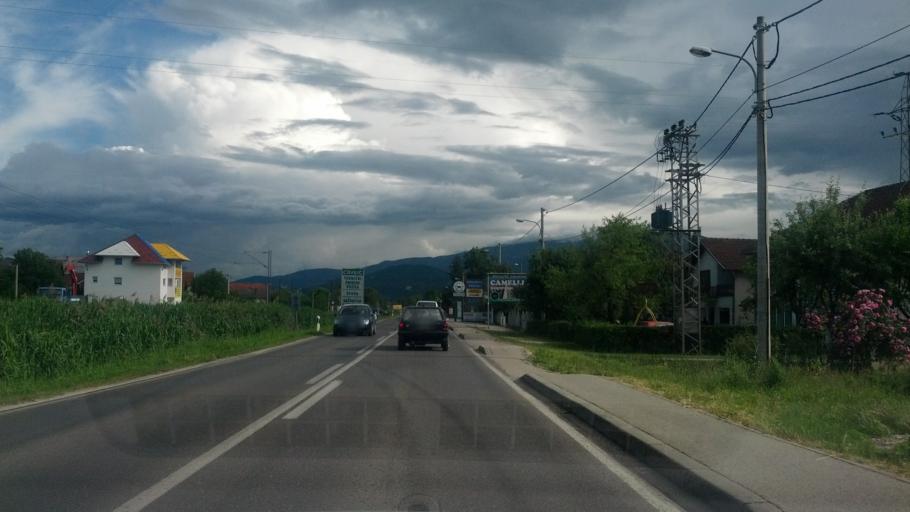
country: BA
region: Federation of Bosnia and Herzegovina
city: Bihac
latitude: 44.8469
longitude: 15.8819
